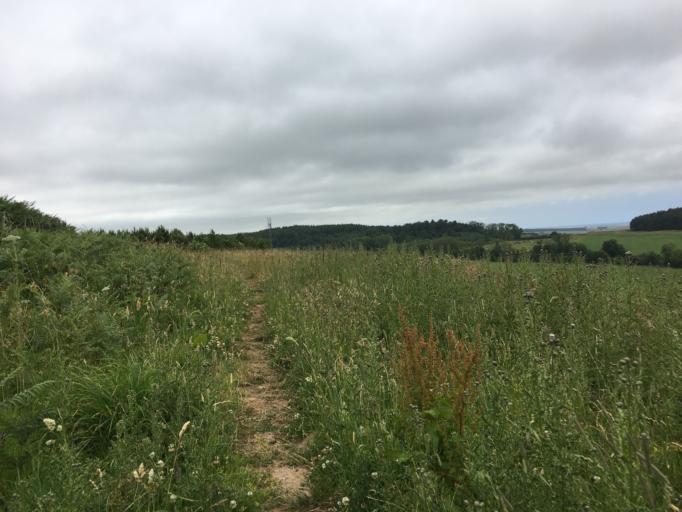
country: GB
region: England
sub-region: Northumberland
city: Belford
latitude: 55.6061
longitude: -1.8614
